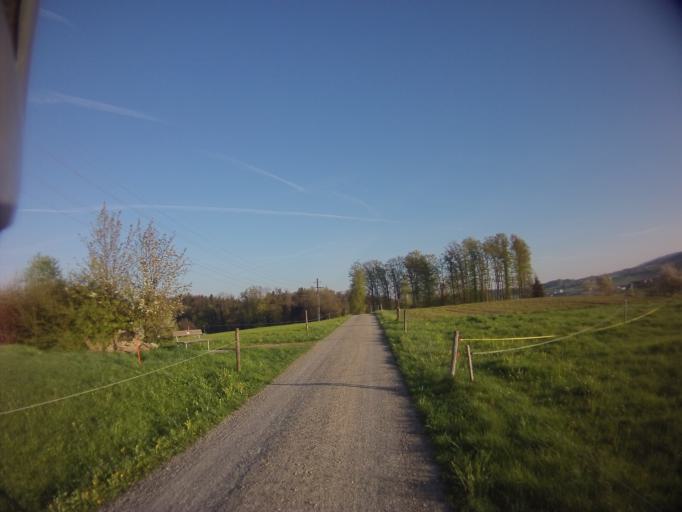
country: CH
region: Zurich
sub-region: Bezirk Affoltern
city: Mettmenstetten
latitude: 47.2374
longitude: 8.4539
